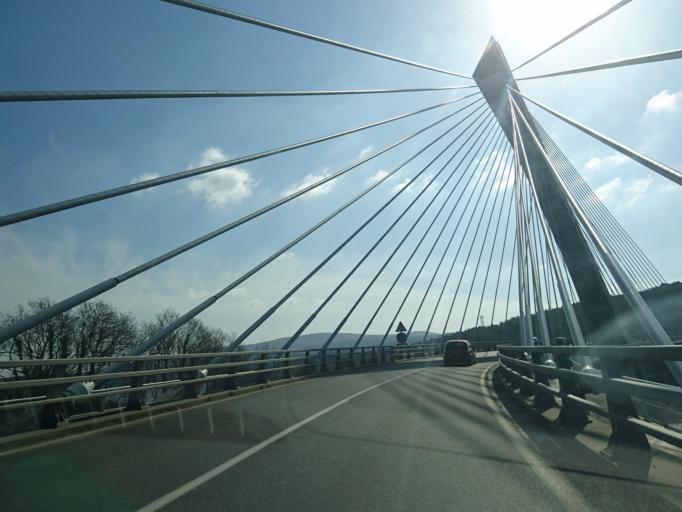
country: FR
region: Brittany
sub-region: Departement du Finistere
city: Hopital-Camfrout
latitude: 48.2713
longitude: -4.2627
